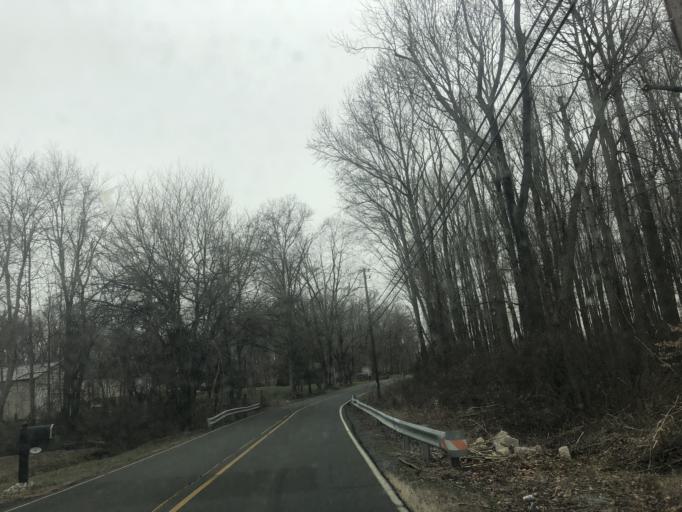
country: US
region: New Jersey
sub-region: Monmouth County
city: Allentown
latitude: 40.1859
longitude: -74.5956
